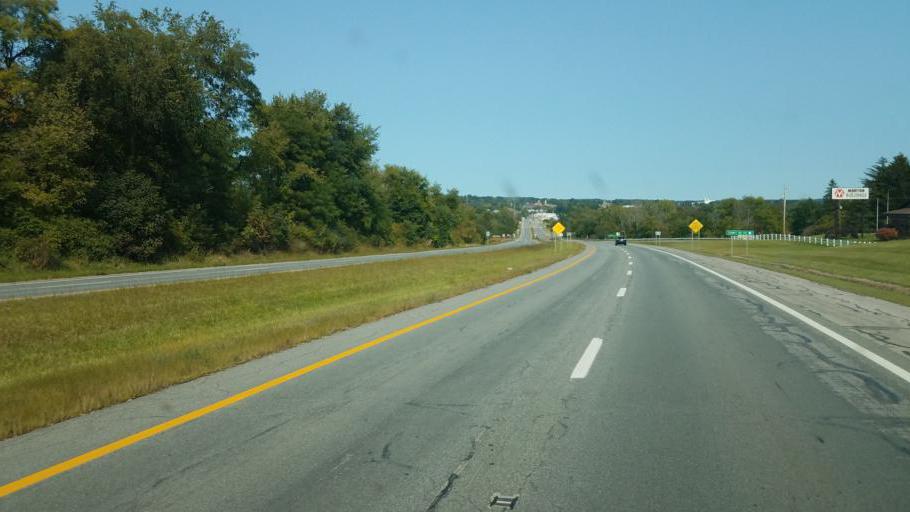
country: US
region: Ohio
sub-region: Wayne County
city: Wooster
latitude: 40.7864
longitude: -81.9604
